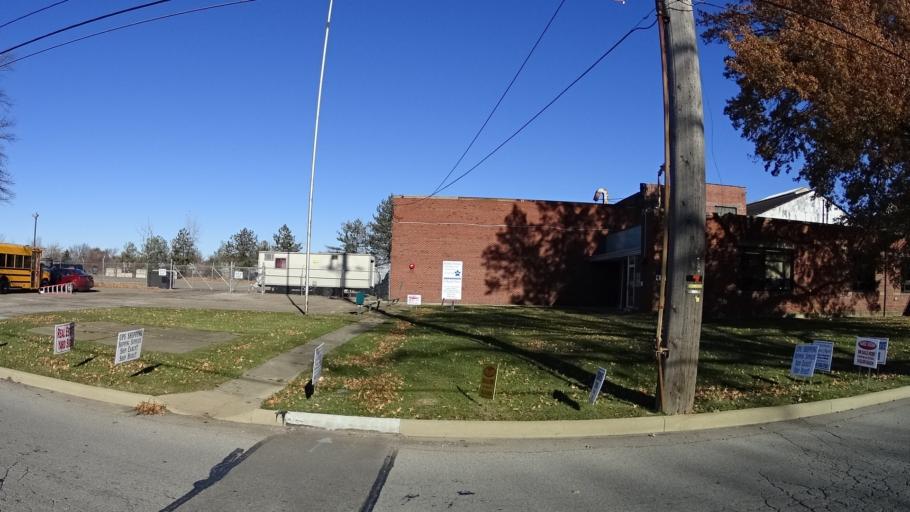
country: US
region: Ohio
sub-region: Lorain County
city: Elyria
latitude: 41.3717
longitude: -82.0813
